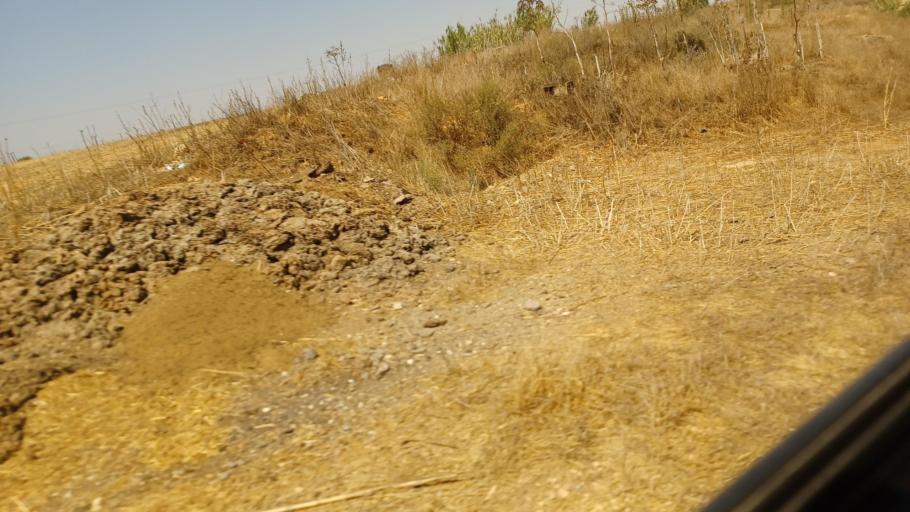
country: CY
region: Ammochostos
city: Acheritou
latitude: 35.0760
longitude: 33.8931
